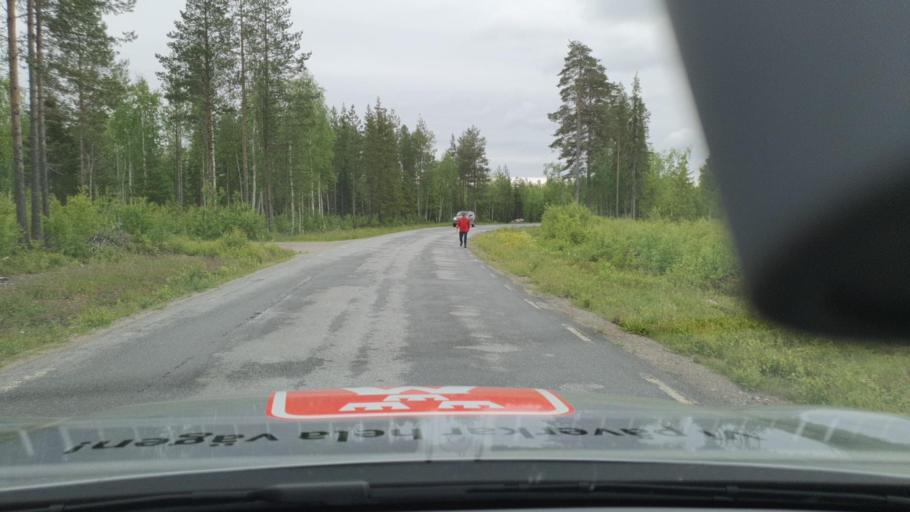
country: SE
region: Norrbotten
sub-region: Lulea Kommun
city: Ranea
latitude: 65.8280
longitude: 22.3204
